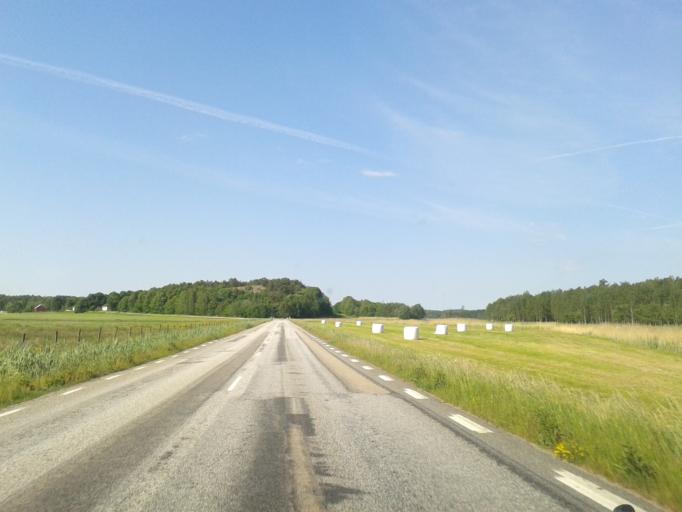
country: SE
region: Vaestra Goetaland
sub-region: Stromstads Kommun
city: Stroemstad
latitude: 58.8595
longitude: 11.2367
